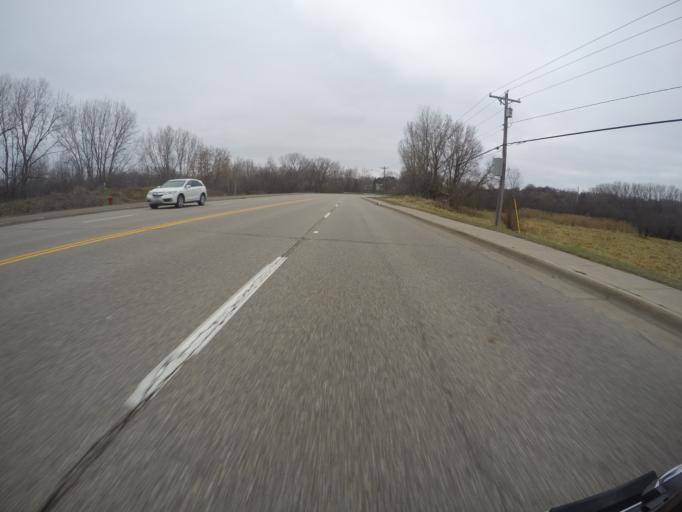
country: US
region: Minnesota
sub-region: Hennepin County
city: Eden Prairie
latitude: 44.8836
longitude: -93.4476
